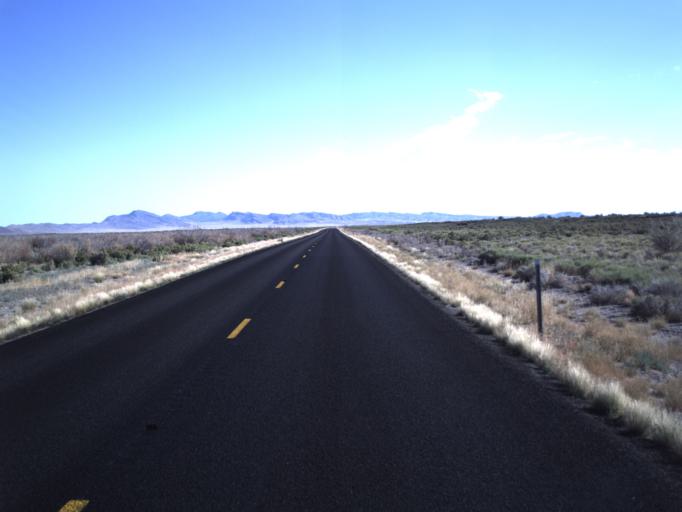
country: US
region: Utah
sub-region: Beaver County
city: Milford
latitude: 38.5861
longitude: -112.9886
